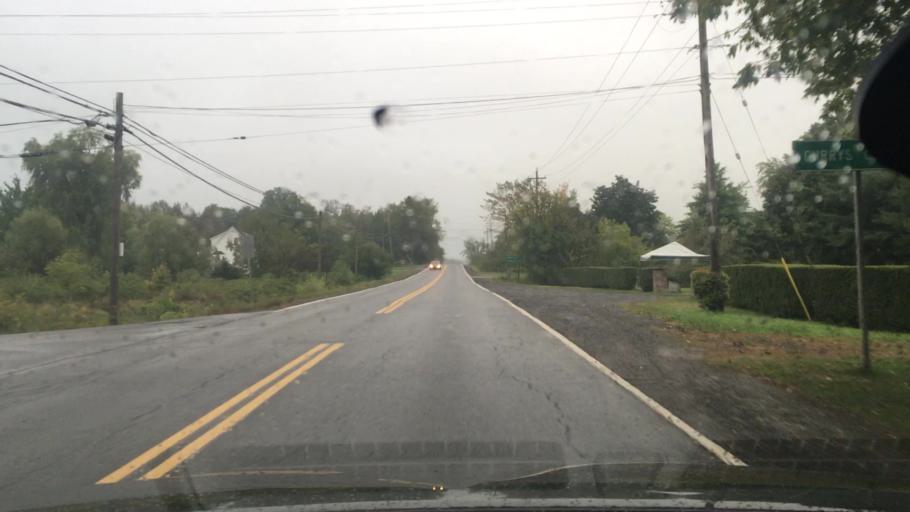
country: CA
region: Nova Scotia
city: Windsor
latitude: 44.9789
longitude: -64.1305
